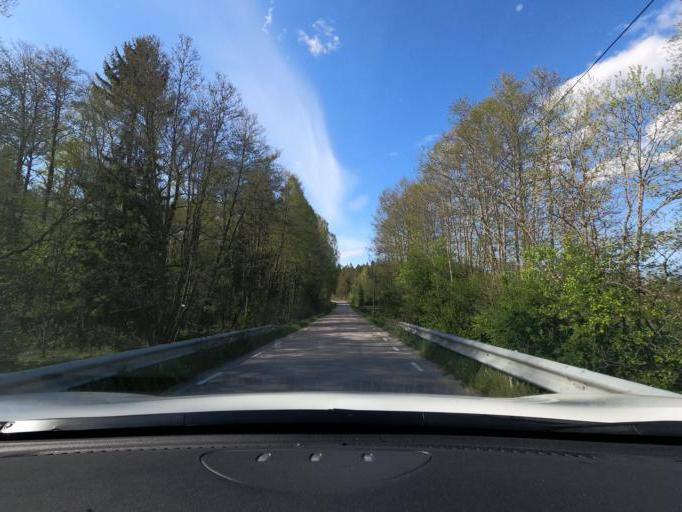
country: SE
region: Vaestra Goetaland
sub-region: Harryda Kommun
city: Ravlanda
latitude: 57.6444
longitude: 12.4982
